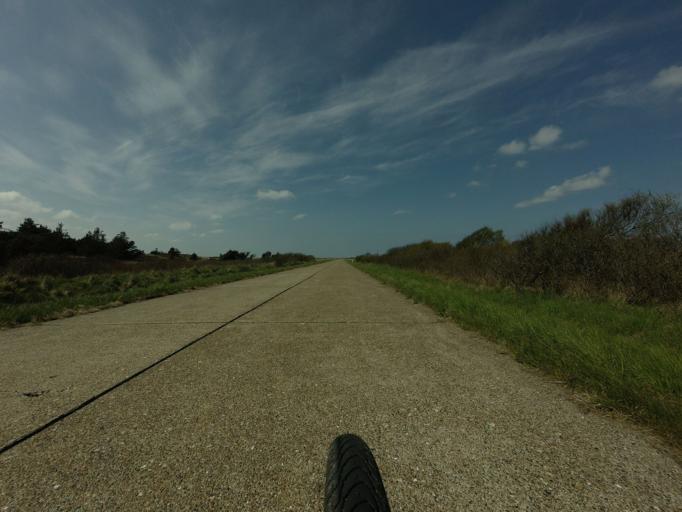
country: DK
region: North Denmark
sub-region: Jammerbugt Kommune
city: Brovst
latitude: 57.1727
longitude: 9.4577
